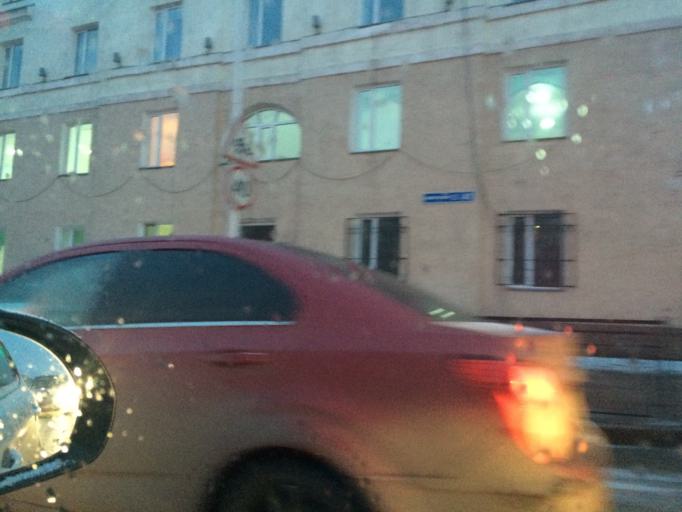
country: KZ
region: Astana Qalasy
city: Astana
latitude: 51.1787
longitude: 71.4178
